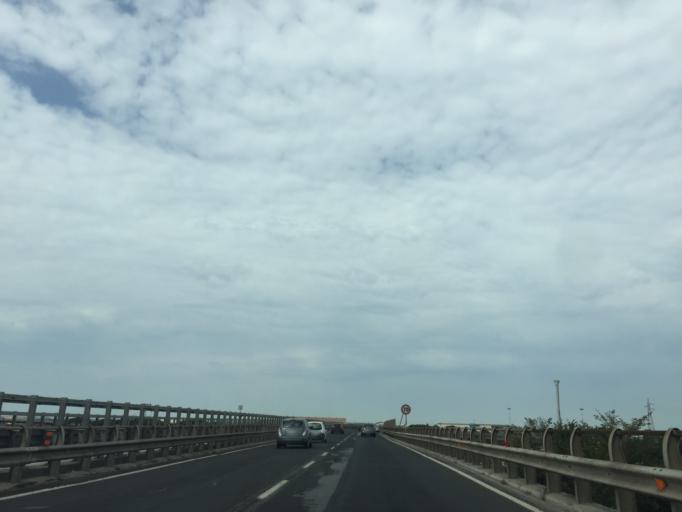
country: IT
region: Tuscany
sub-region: Province of Pisa
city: Pisa
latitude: 43.7000
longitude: 10.3943
